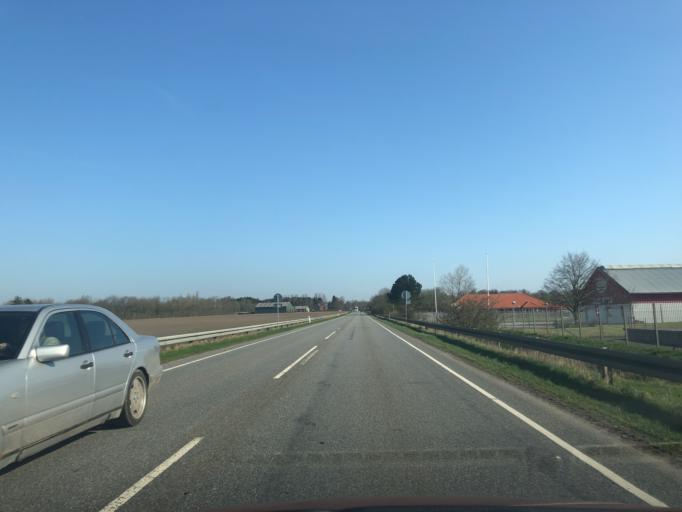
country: DK
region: Zealand
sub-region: Faxe Kommune
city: Haslev
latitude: 55.3309
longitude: 11.9421
